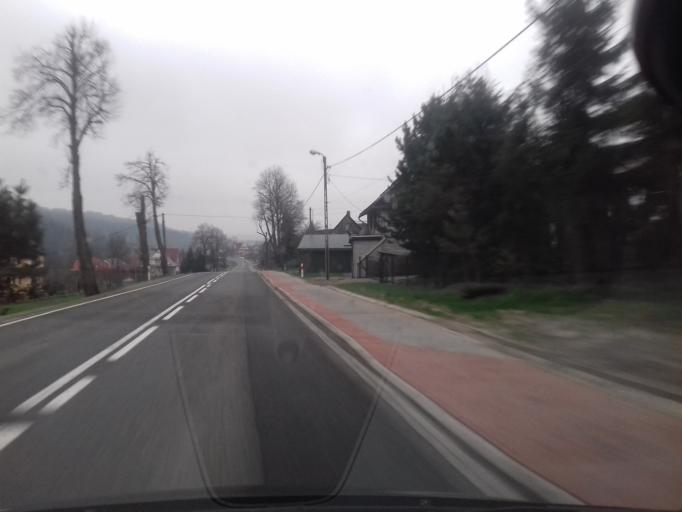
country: PL
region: Lesser Poland Voivodeship
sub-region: Powiat limanowski
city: Mszana Gorna
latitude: 49.6938
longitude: 20.1199
